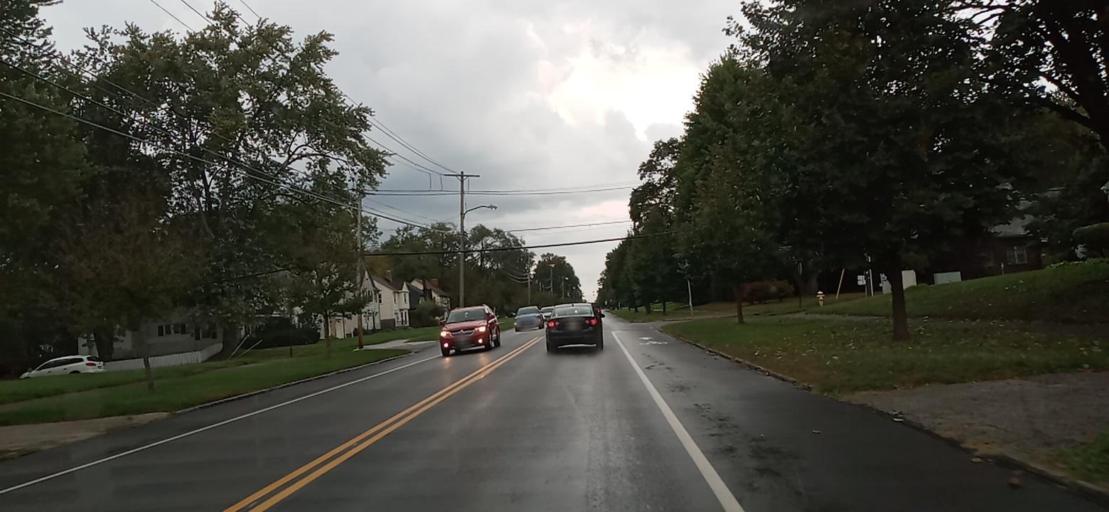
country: US
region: Ohio
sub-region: Summit County
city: Akron
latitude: 41.0901
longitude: -81.5694
